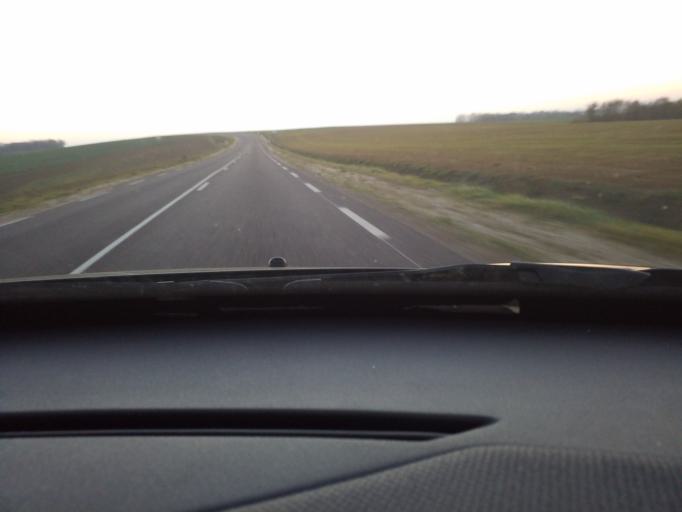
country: FR
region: Franche-Comte
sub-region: Departement de la Haute-Saone
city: Faverney
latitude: 47.9051
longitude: 6.0824
